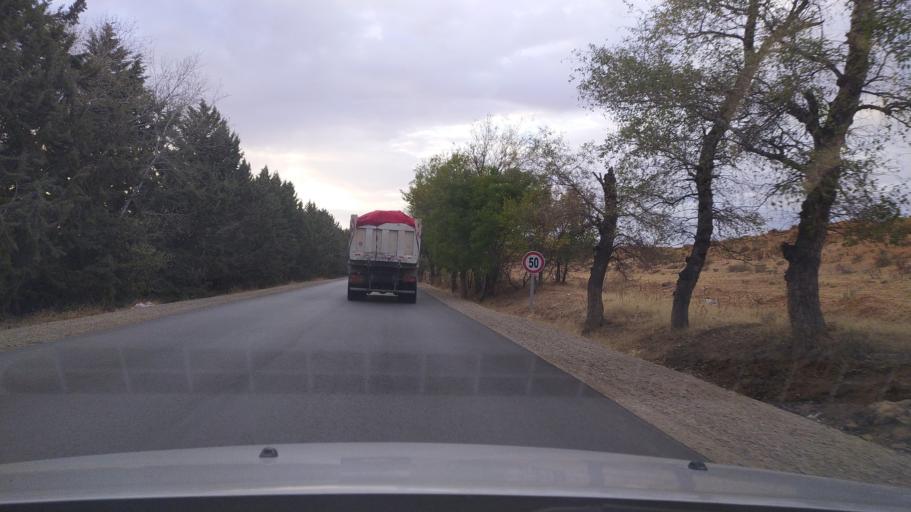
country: DZ
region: Tiaret
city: Frenda
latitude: 35.0496
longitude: 1.0772
